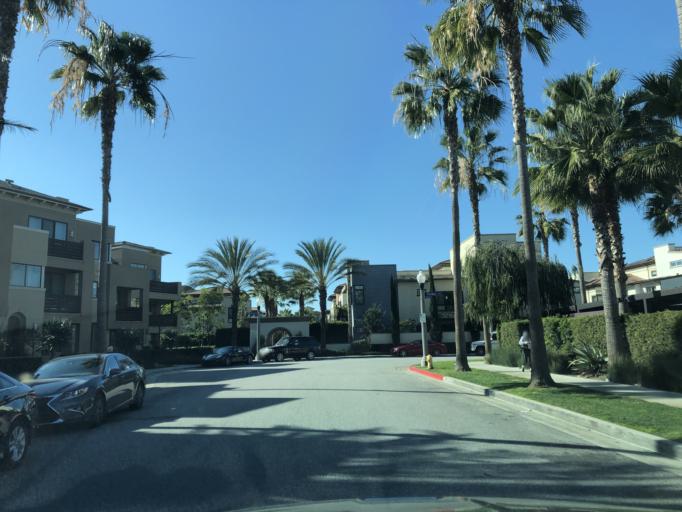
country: US
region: California
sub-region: Los Angeles County
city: Marina del Rey
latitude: 33.9749
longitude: -118.4190
